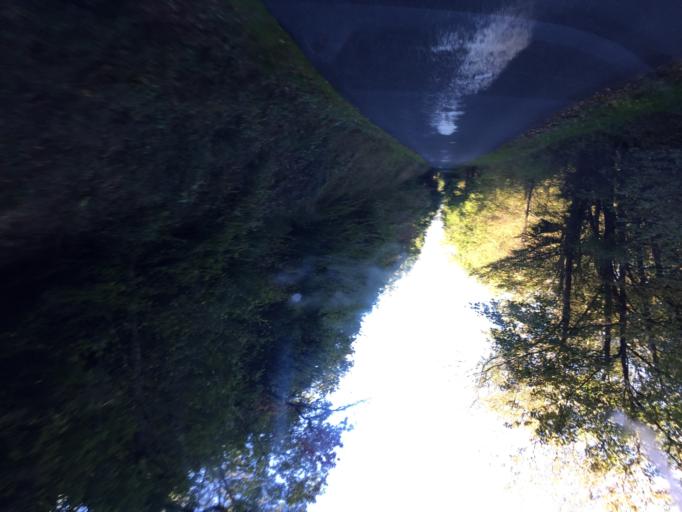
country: FR
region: Rhone-Alpes
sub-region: Departement du Rhone
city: Le Perreon
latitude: 46.0277
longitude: 4.5671
